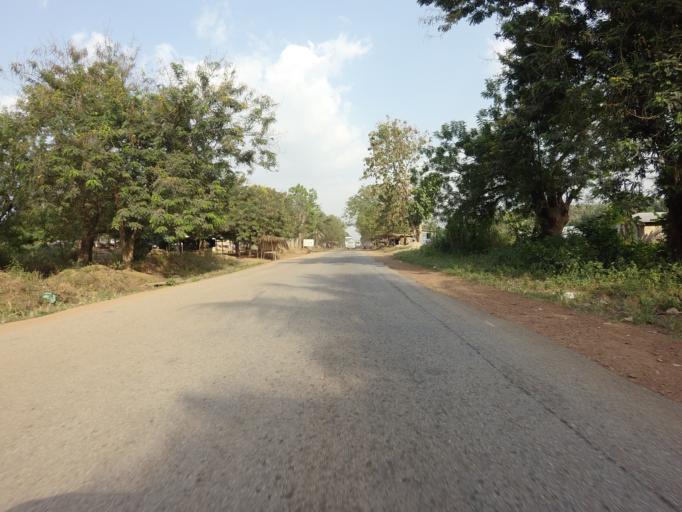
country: GH
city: Akropong
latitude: 6.2408
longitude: 0.1078
